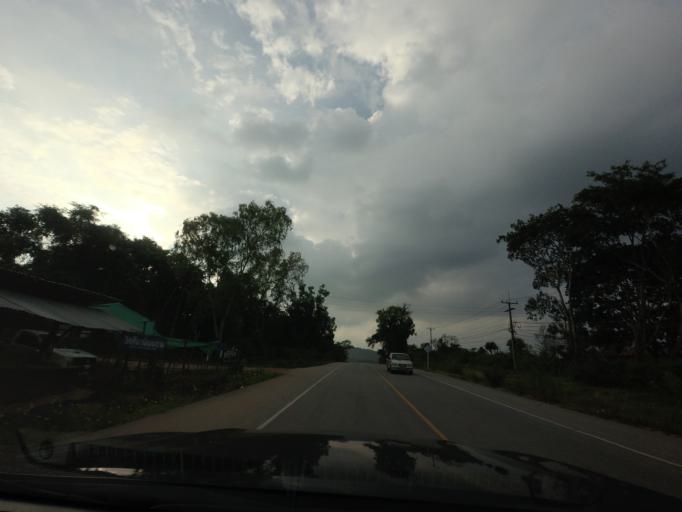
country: TH
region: Loei
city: Dan Sai
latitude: 17.3292
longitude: 101.0988
